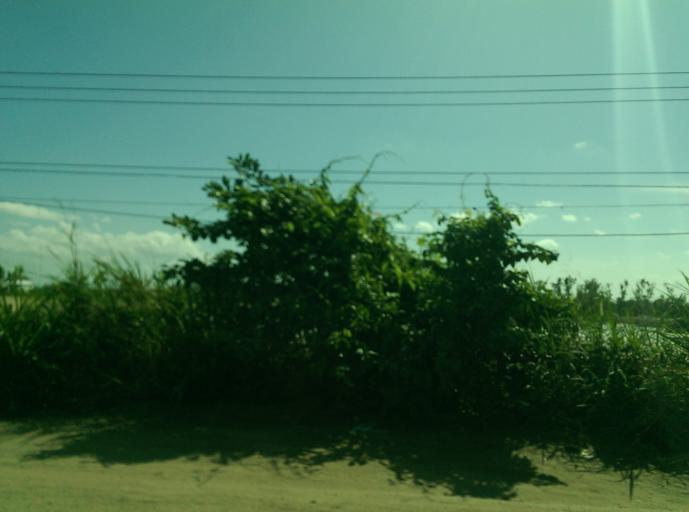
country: MX
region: Tabasco
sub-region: Centro
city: Anacleto Canabal 2da. Seccion
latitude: 17.9829
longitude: -93.0156
